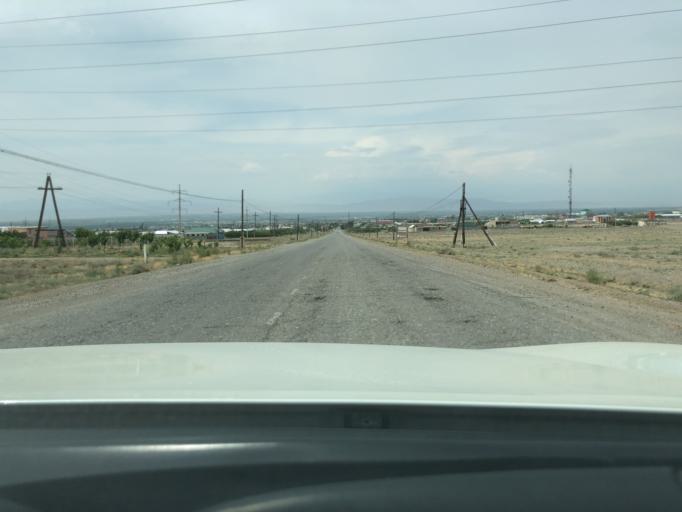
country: TJ
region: Viloyati Sughd
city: Konibodom
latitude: 40.2676
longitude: 70.4517
